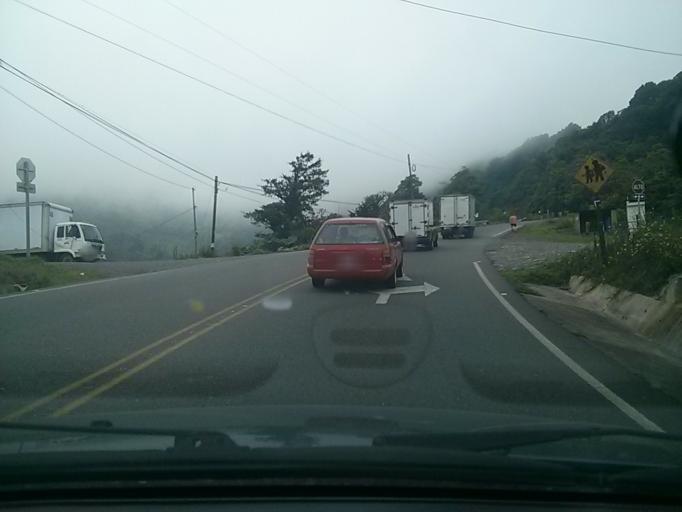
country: CR
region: Cartago
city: Tobosi
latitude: 9.7424
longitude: -83.9595
